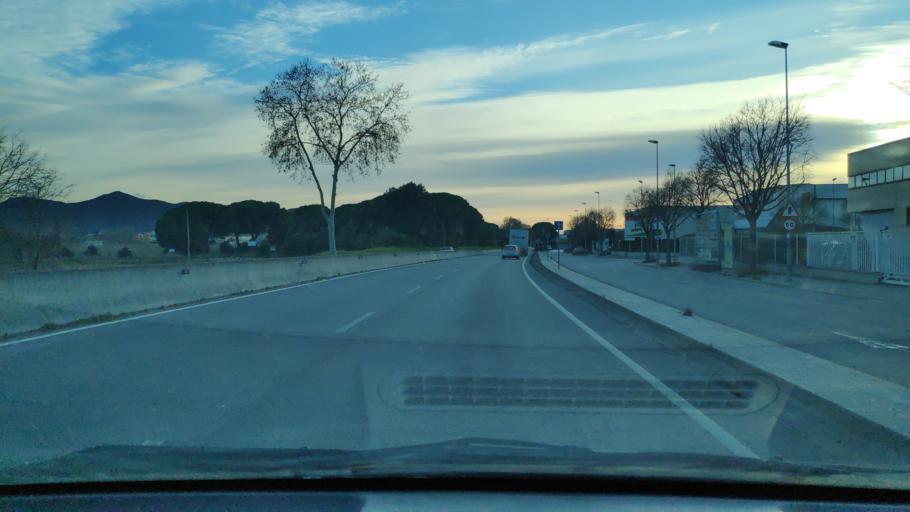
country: ES
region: Catalonia
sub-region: Provincia de Barcelona
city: Llica de Vall
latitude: 41.5715
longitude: 2.2701
